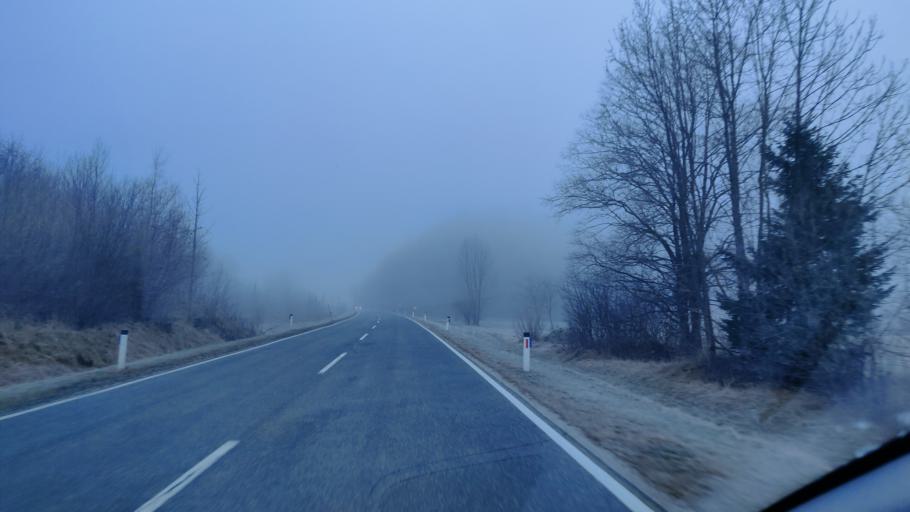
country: SI
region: Bohinj
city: Bohinjska Bistrica
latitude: 46.2888
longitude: 14.0111
